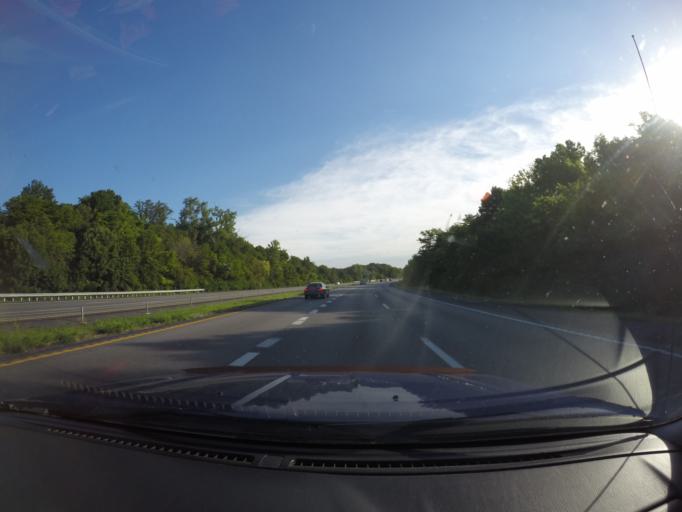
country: US
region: Missouri
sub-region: Platte County
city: Riverside
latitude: 39.1844
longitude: -94.6215
